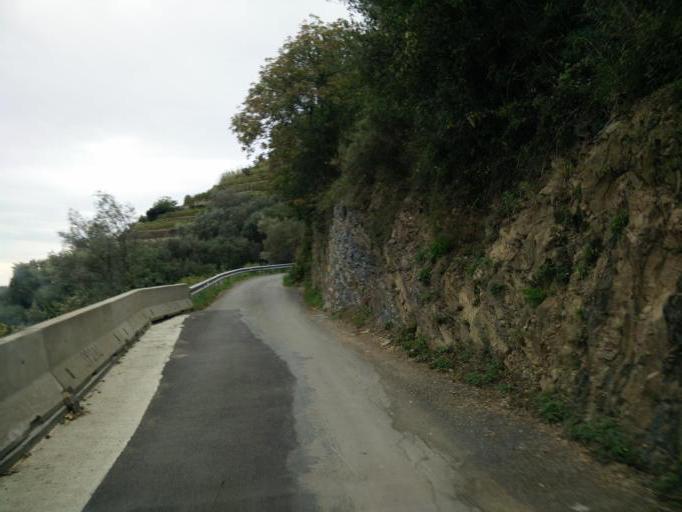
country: IT
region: Liguria
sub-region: Provincia di La Spezia
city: Vernazza
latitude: 44.1395
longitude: 9.6899
